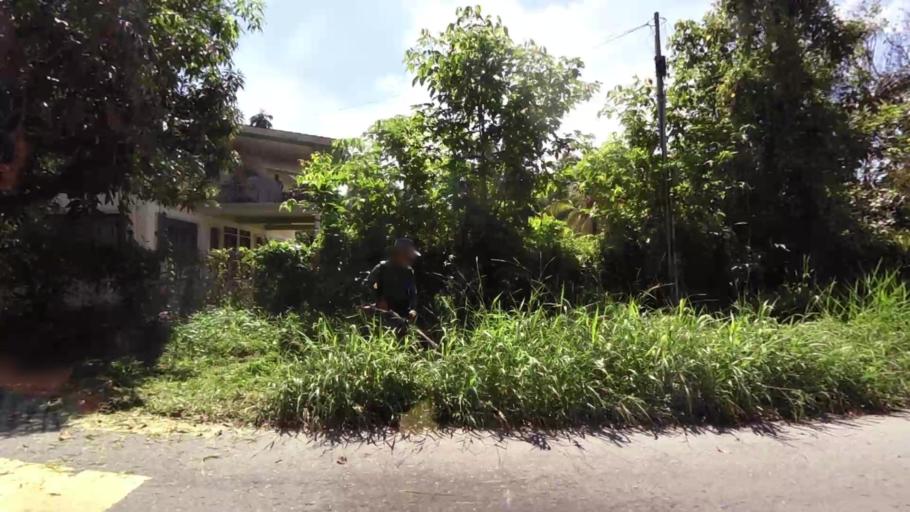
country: BN
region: Brunei and Muara
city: Bandar Seri Begawan
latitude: 4.9413
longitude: 114.9478
